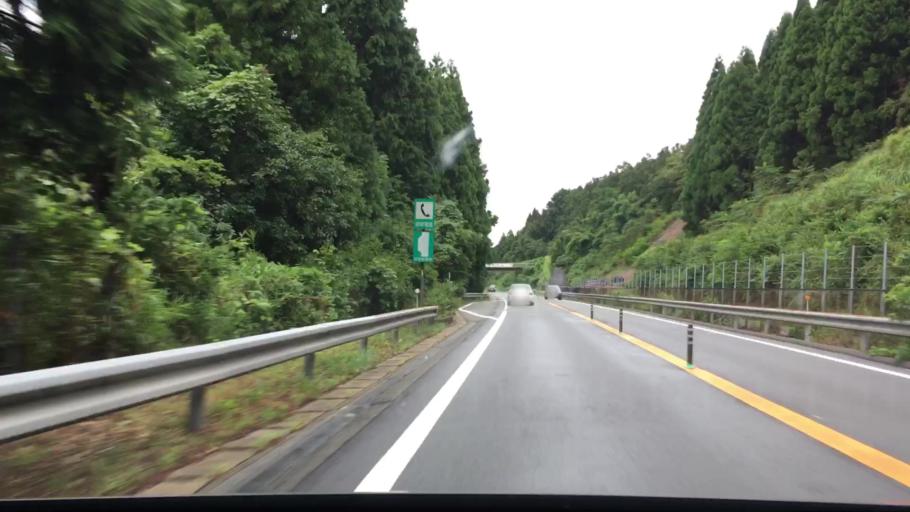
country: JP
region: Hyogo
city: Nishiwaki
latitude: 35.1045
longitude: 134.7781
